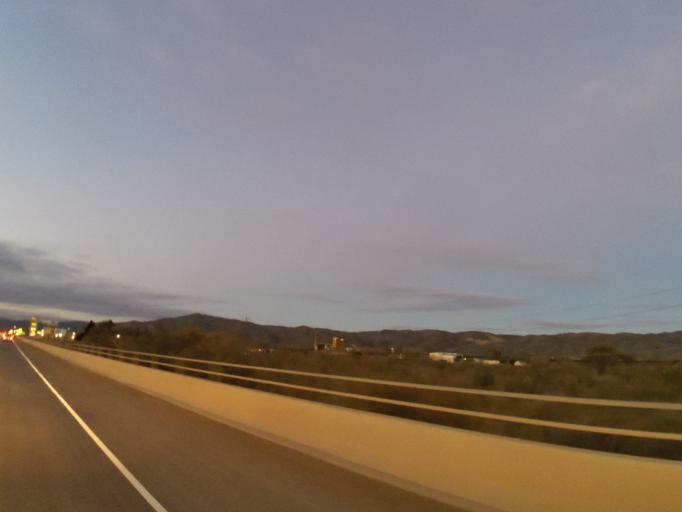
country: US
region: California
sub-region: Monterey County
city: Soledad
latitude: 36.4095
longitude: -121.3191
